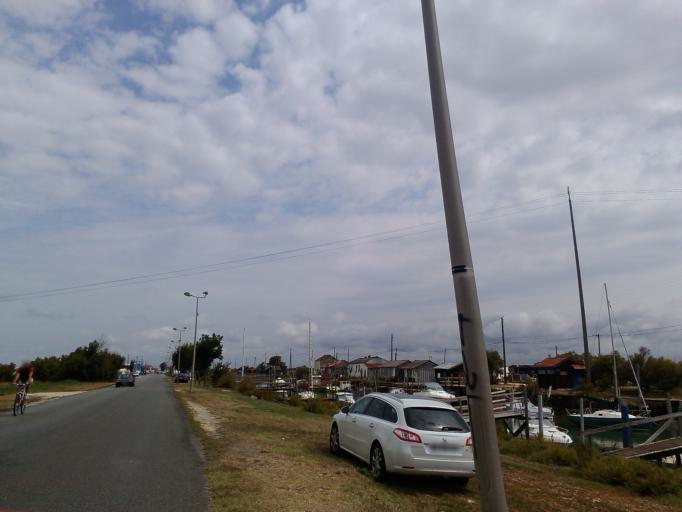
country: FR
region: Poitou-Charentes
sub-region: Departement de la Charente-Maritime
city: La Tremblade
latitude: 45.7719
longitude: -1.1316
